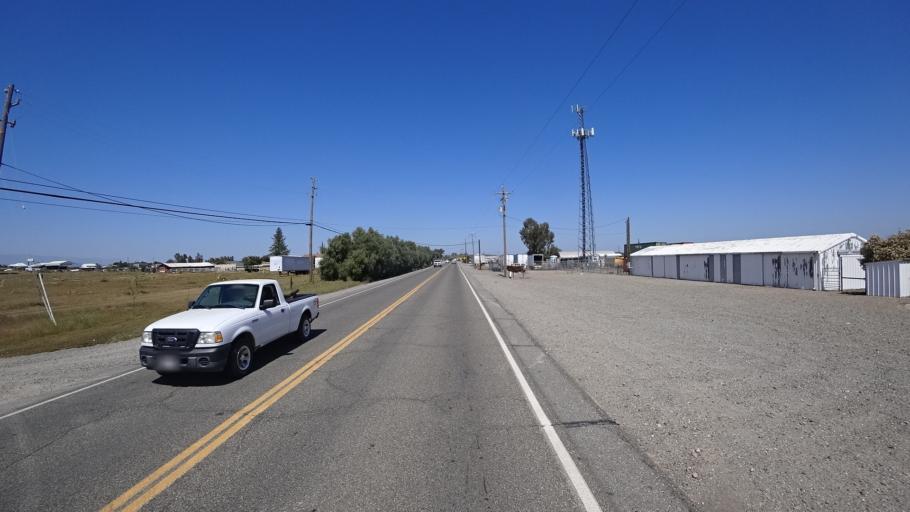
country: US
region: California
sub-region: Glenn County
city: Orland
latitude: 39.6933
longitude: -122.1966
